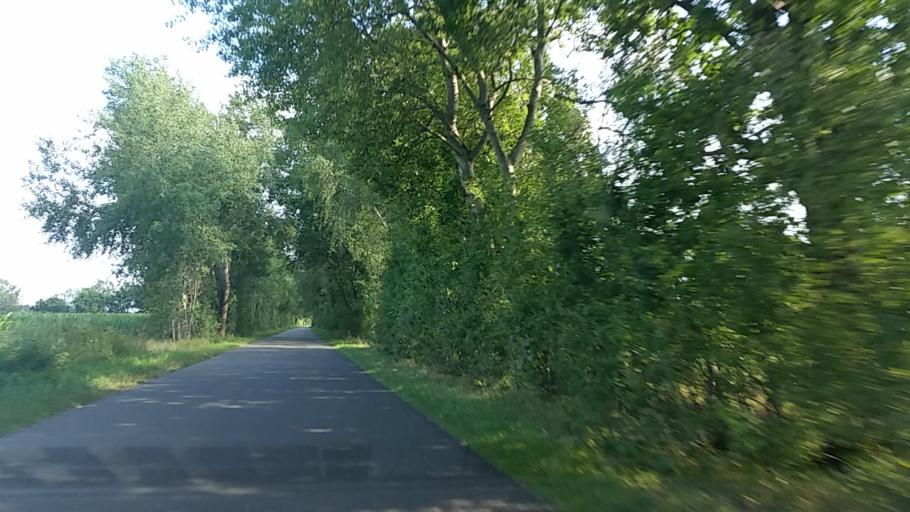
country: DE
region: Lower Saxony
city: Winsen
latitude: 53.3305
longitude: 10.2421
